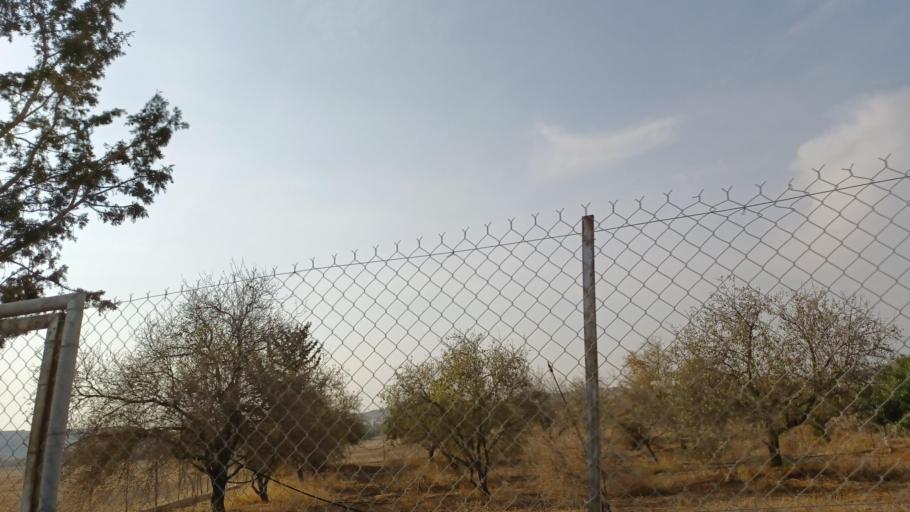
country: CY
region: Larnaka
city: Troulloi
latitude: 35.0332
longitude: 33.6045
